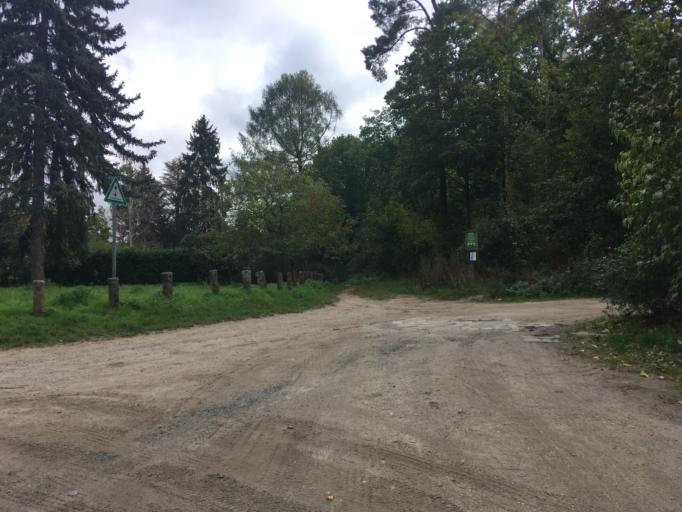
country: DE
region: Berlin
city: Kladow
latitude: 52.4565
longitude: 13.1328
